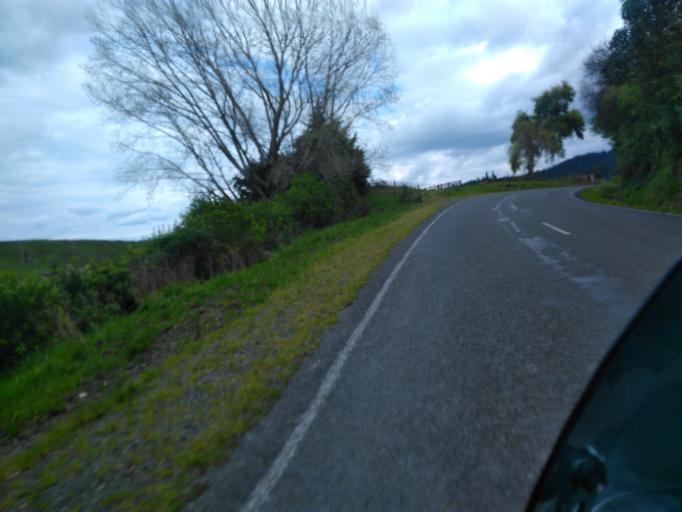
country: NZ
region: Hawke's Bay
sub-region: Wairoa District
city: Wairoa
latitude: -38.8791
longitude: 177.4945
